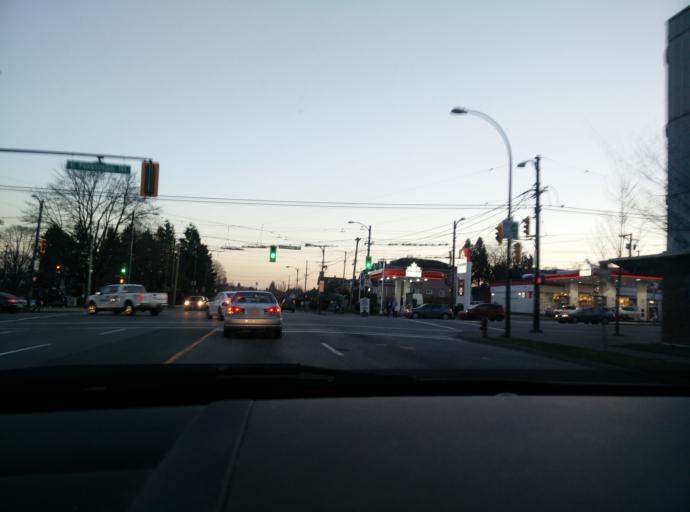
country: CA
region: British Columbia
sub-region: Fraser Valley Regional District
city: North Vancouver
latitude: 49.2815
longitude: -123.0441
